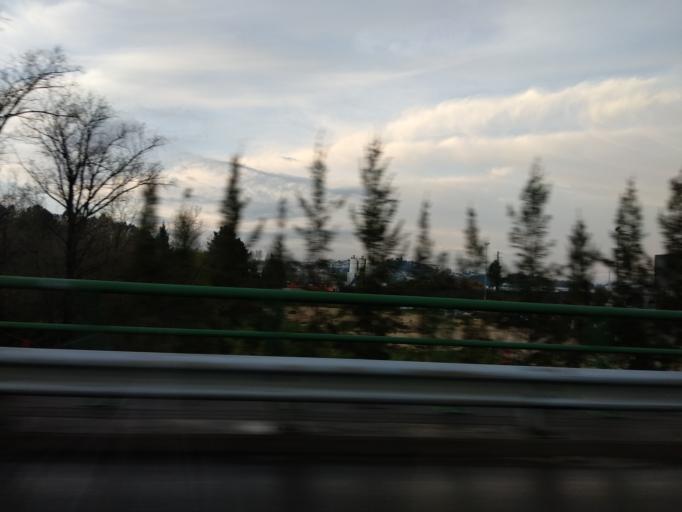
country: PT
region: Braga
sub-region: Braga
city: Oliveira
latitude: 41.5078
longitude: -8.4571
